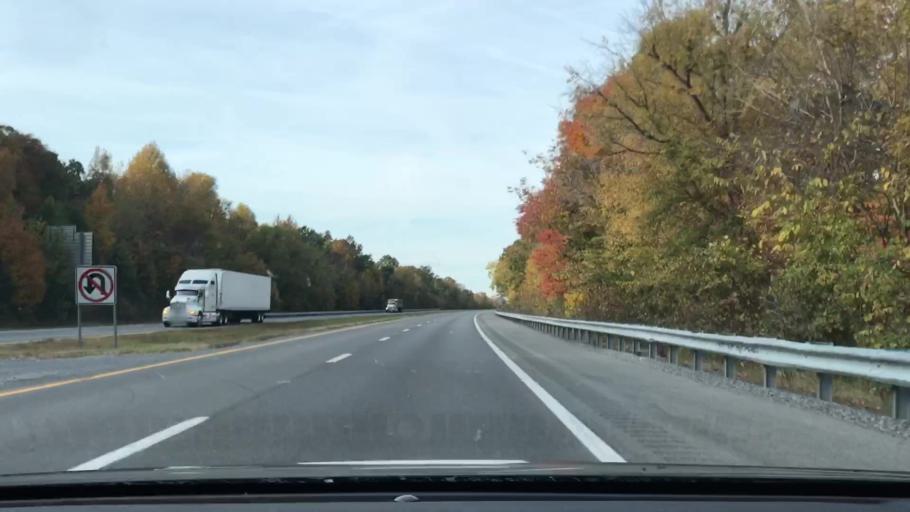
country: US
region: Kentucky
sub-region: Marshall County
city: Benton
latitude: 36.8409
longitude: -88.4175
